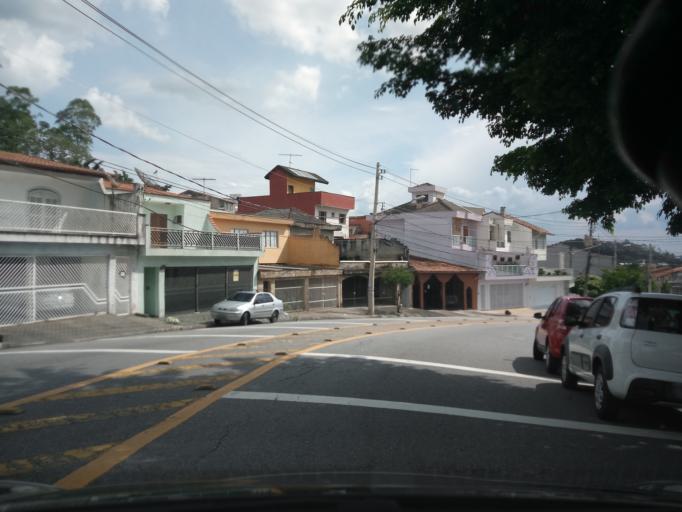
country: BR
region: Sao Paulo
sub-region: Sao Bernardo Do Campo
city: Sao Bernardo do Campo
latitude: -23.7470
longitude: -46.5464
